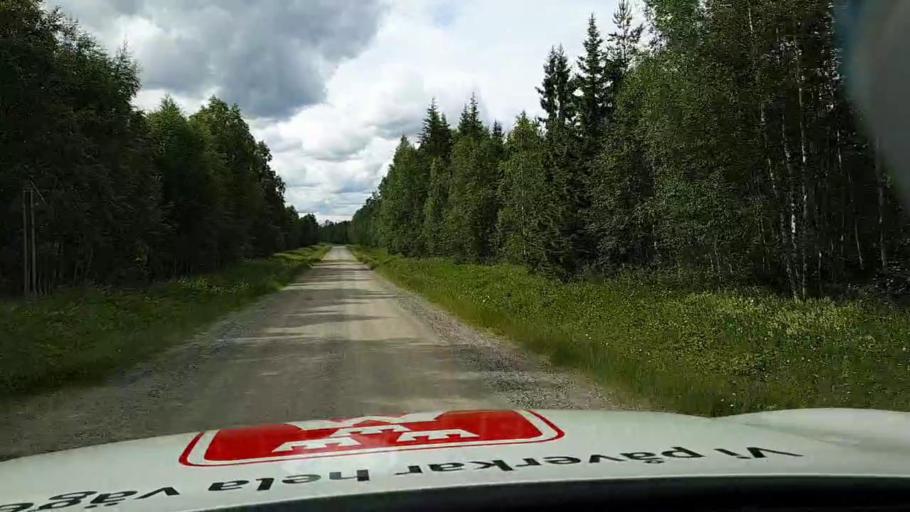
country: SE
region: Jaemtland
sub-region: Stroemsunds Kommun
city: Stroemsund
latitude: 63.3107
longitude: 15.5283
